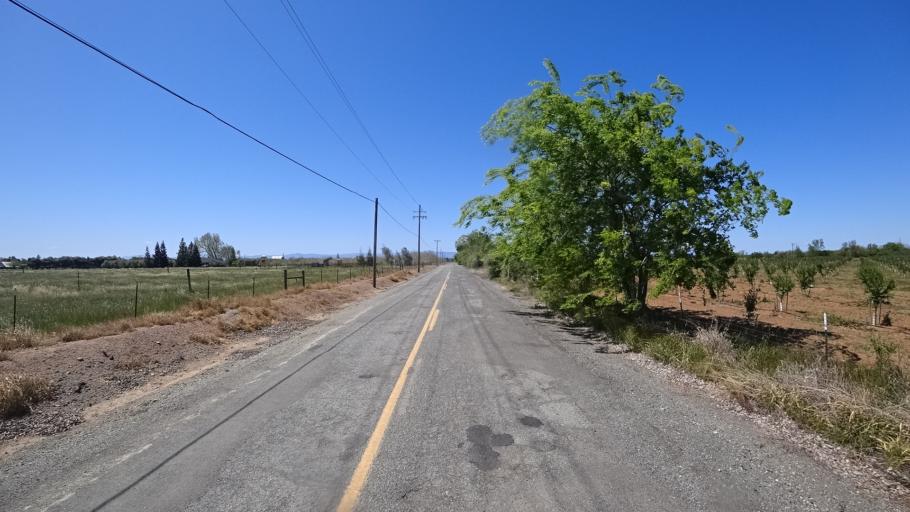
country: US
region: California
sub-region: Glenn County
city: Orland
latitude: 39.7893
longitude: -122.2078
